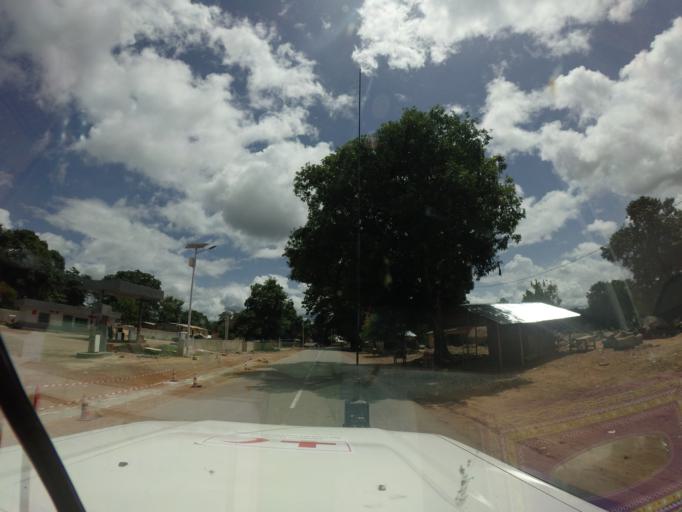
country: SL
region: Northern Province
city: Bindi
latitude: 10.1708
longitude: -11.4093
